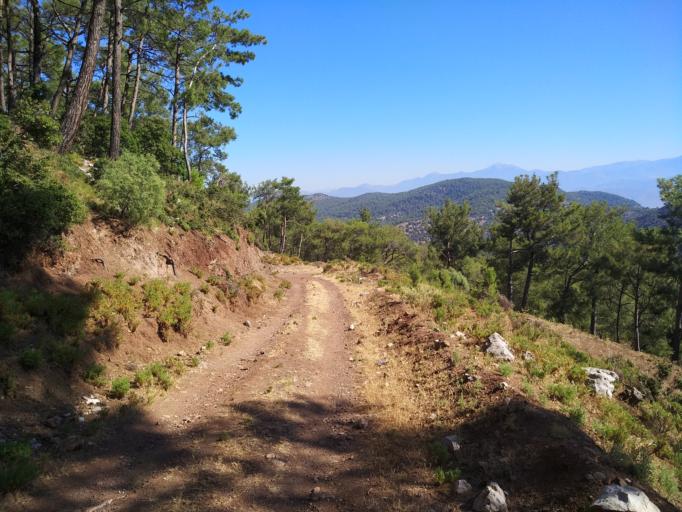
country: TR
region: Mugla
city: OEluedeniz
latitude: 36.5702
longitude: 29.1187
